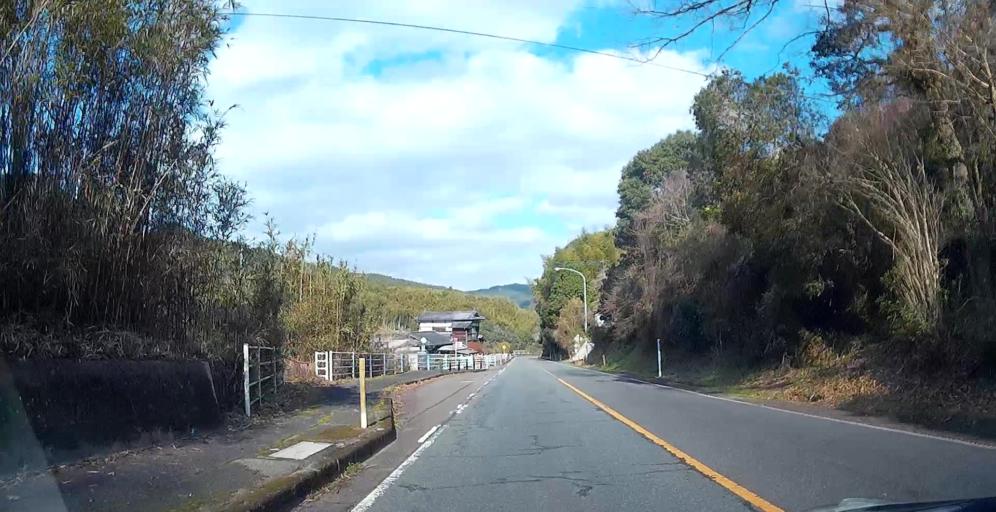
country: JP
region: Kumamoto
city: Yatsushiro
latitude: 32.3931
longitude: 130.5449
